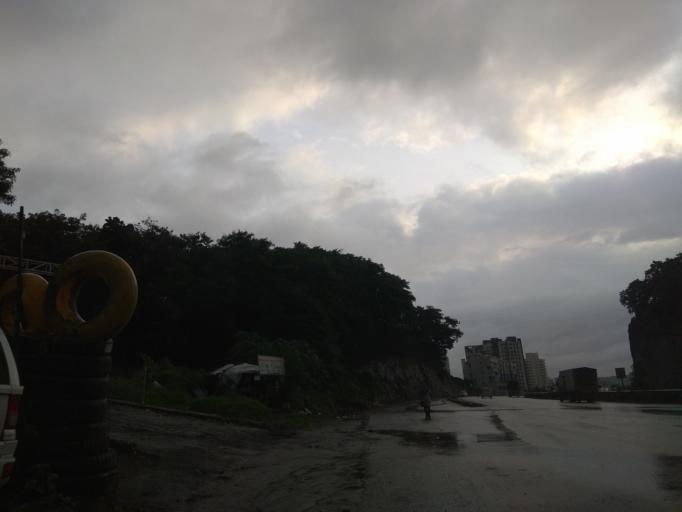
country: IN
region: Maharashtra
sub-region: Pune Division
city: Kharakvasla
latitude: 18.4961
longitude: 73.7877
